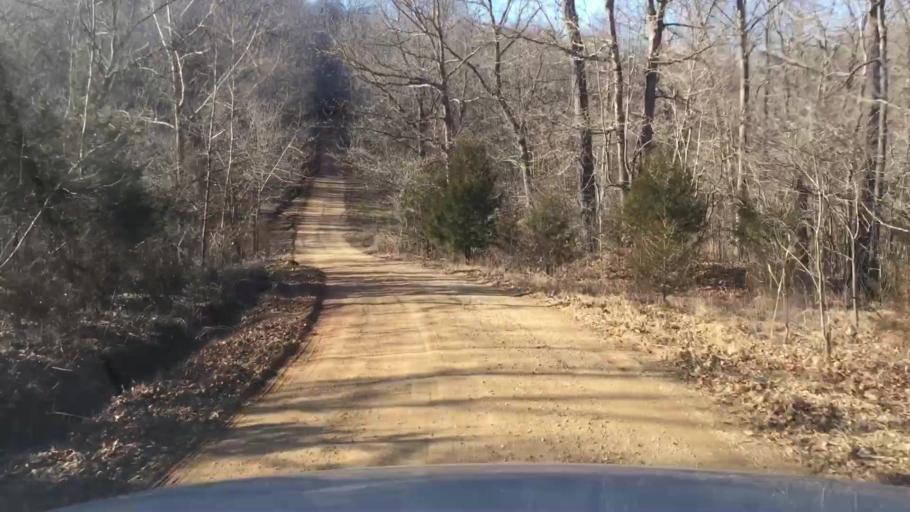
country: US
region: Missouri
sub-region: Morgan County
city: Versailles
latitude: 38.3240
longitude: -92.7652
